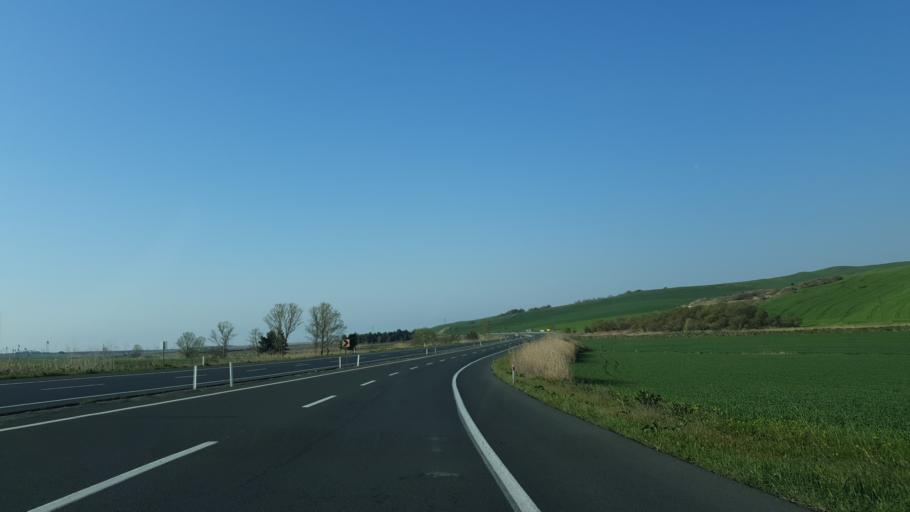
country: TR
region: Tekirdag
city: Corlu
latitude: 41.0536
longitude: 27.7373
